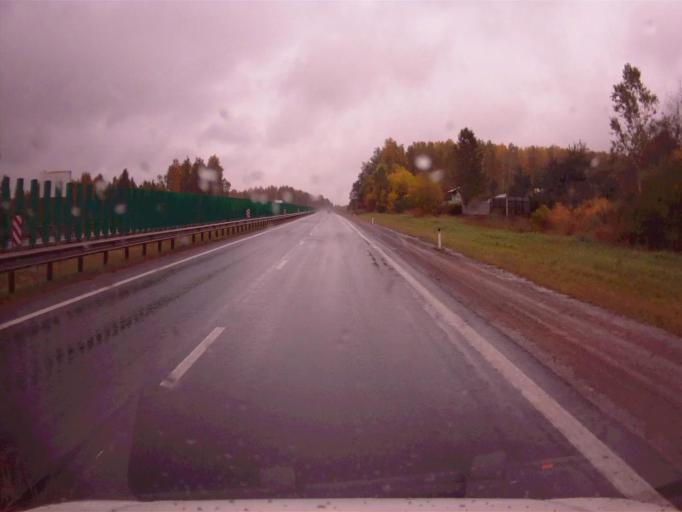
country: RU
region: Chelyabinsk
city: Dolgoderevenskoye
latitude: 55.3306
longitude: 61.3206
